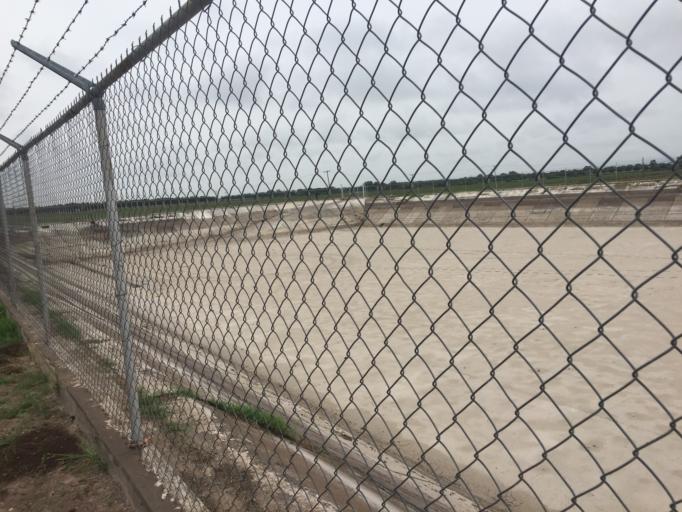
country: MX
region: Coahuila
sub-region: Matamoros
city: Veinte de Noviembre
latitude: 25.7220
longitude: -103.3615
